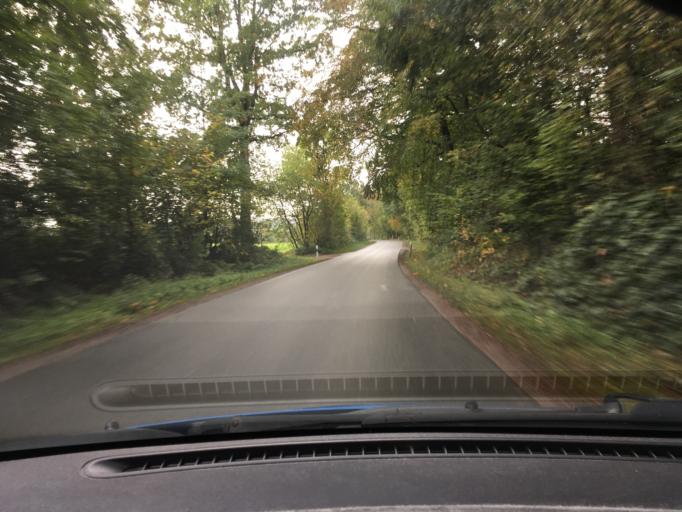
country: DE
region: Schleswig-Holstein
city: Stocksee
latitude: 54.0647
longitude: 10.3572
